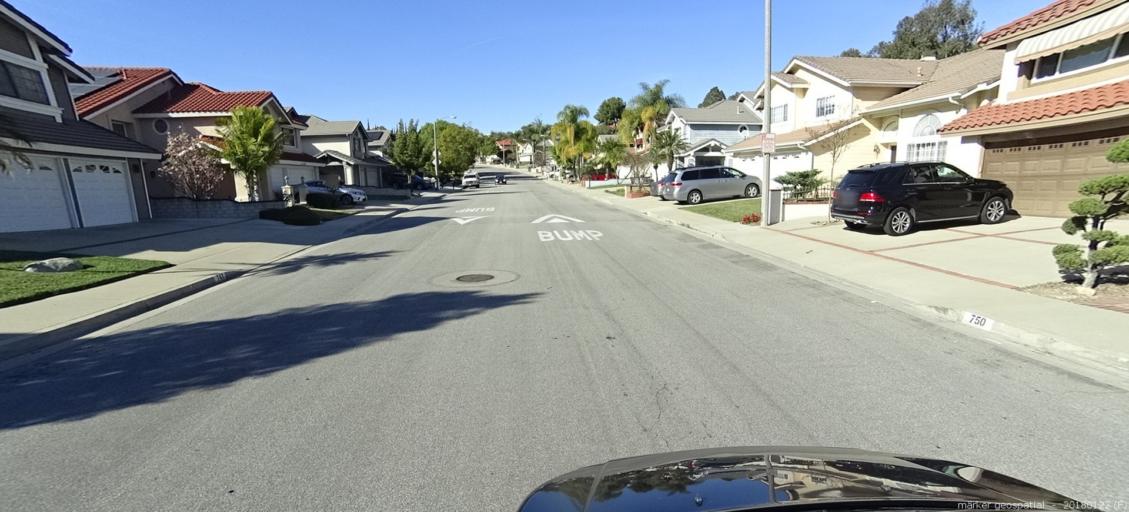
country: US
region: California
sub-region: Los Angeles County
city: Diamond Bar
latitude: 34.0141
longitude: -117.7953
